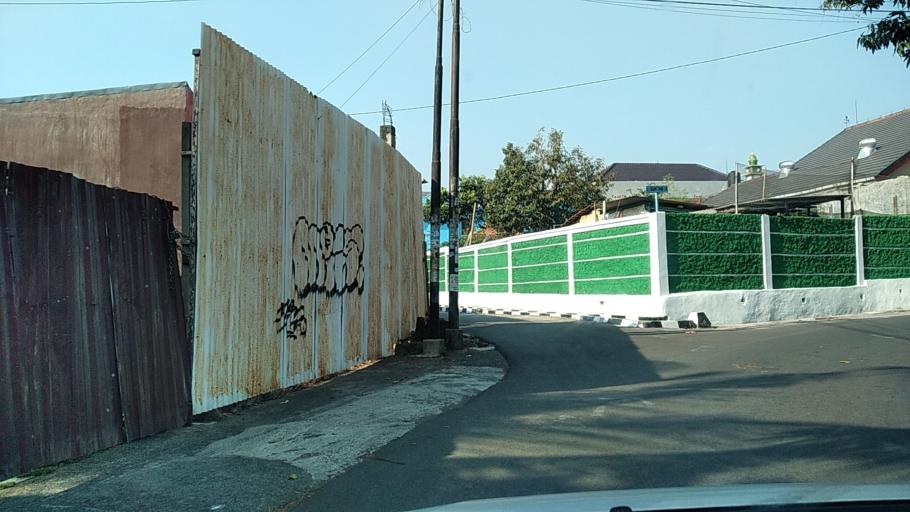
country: ID
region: Central Java
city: Ungaran
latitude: -7.0693
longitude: 110.4274
